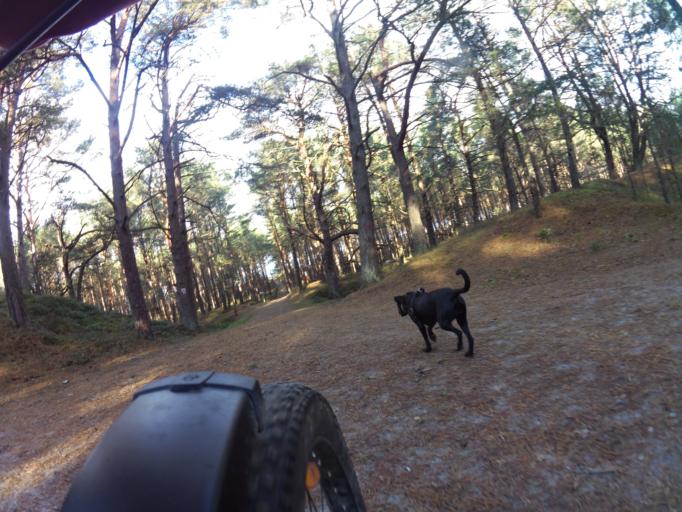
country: PL
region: Pomeranian Voivodeship
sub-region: Powiat wejherowski
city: Choczewo
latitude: 54.8036
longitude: 17.7894
